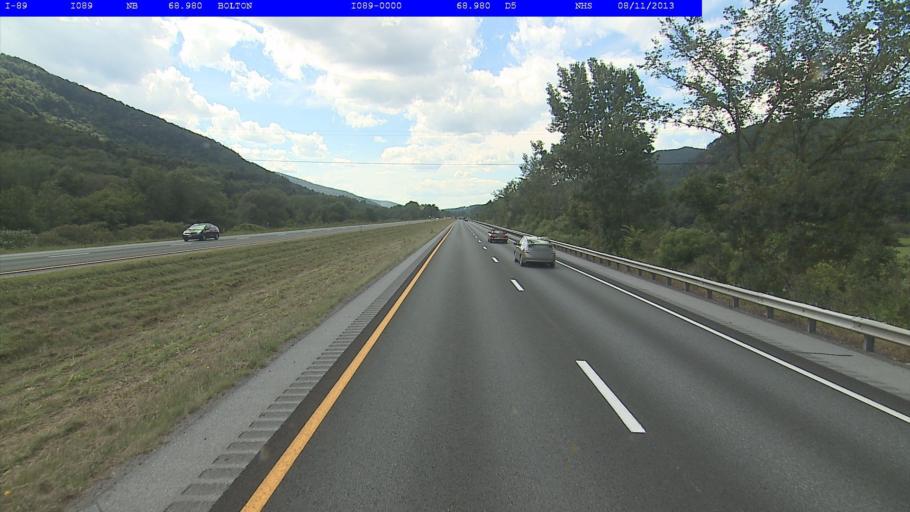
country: US
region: Vermont
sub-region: Washington County
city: Waterbury
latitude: 44.3649
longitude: -72.8489
